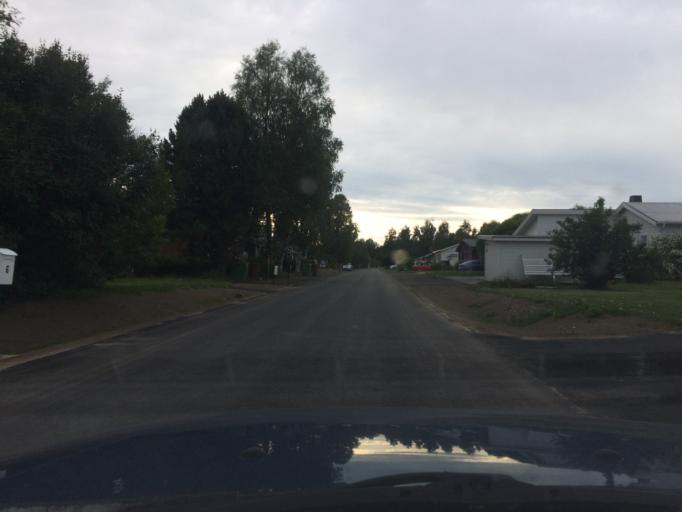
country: SE
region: Norrbotten
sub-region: Pitea Kommun
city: Pitea
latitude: 65.3261
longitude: 21.4488
